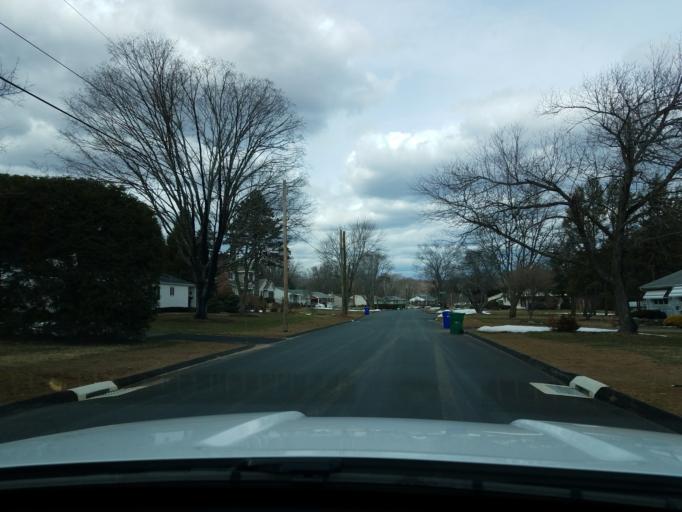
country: US
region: Connecticut
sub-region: Hartford County
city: Manchester
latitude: 41.8231
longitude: -72.5176
